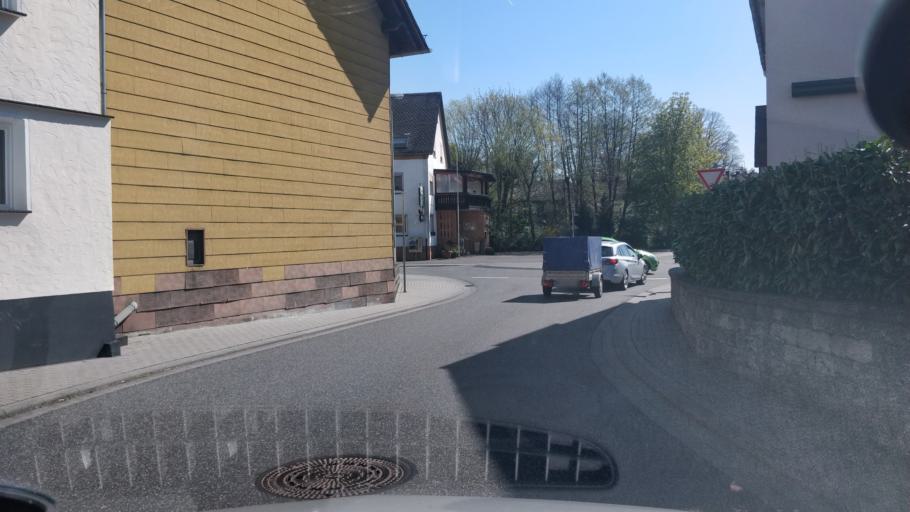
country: DE
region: Hesse
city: Waldbrunn
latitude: 50.5244
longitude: 8.0939
